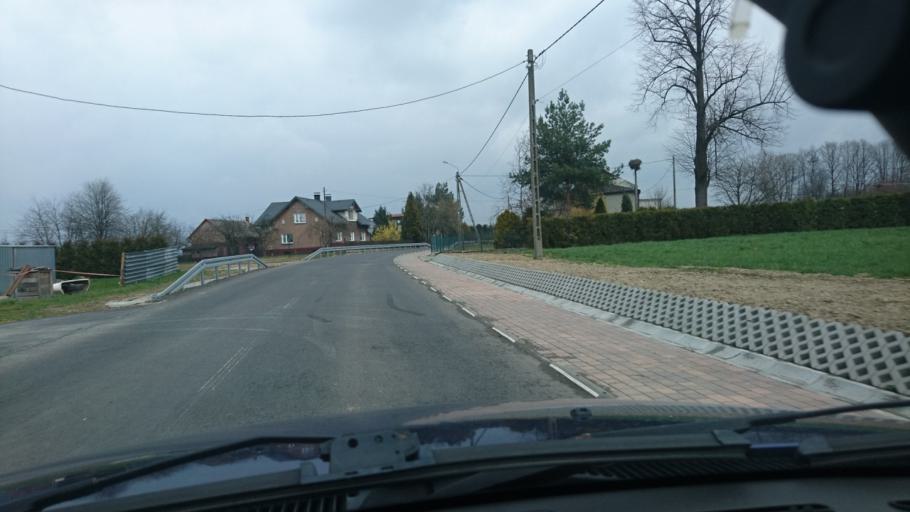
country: PL
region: Silesian Voivodeship
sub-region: Powiat bielski
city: Bronow
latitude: 49.8796
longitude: 18.9266
